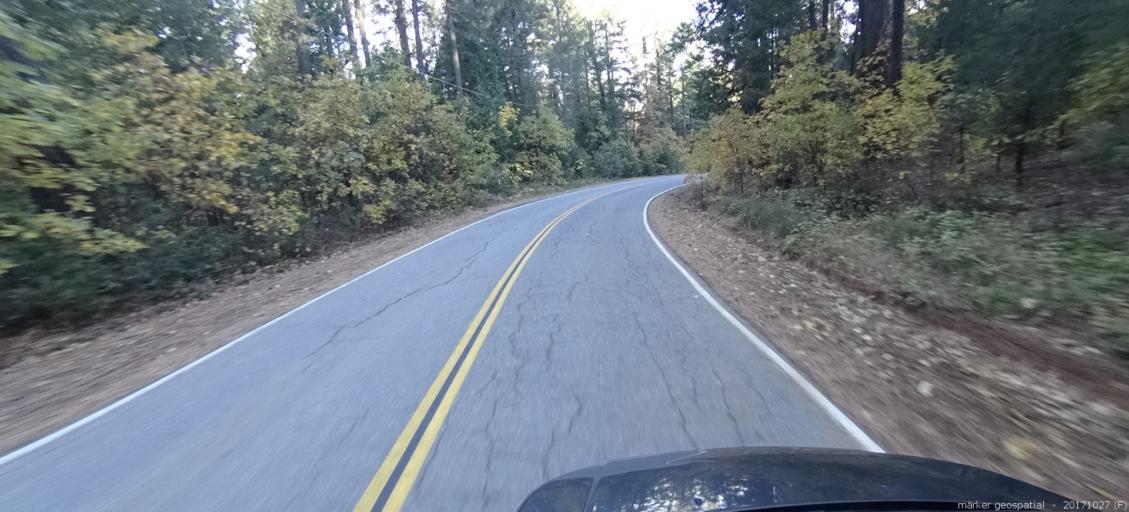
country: US
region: California
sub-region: Shasta County
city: Burney
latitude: 40.9924
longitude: -121.9204
